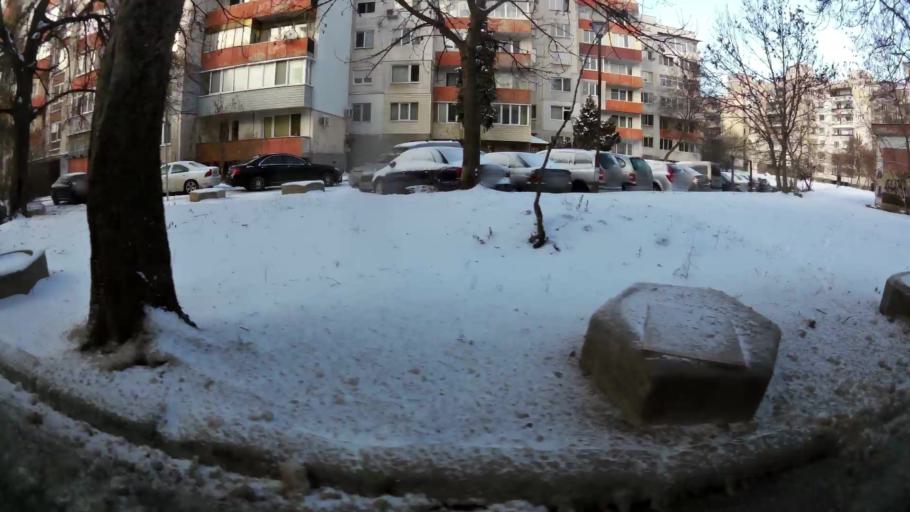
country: BG
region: Sofia-Capital
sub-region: Stolichna Obshtina
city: Sofia
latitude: 42.6681
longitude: 23.3208
